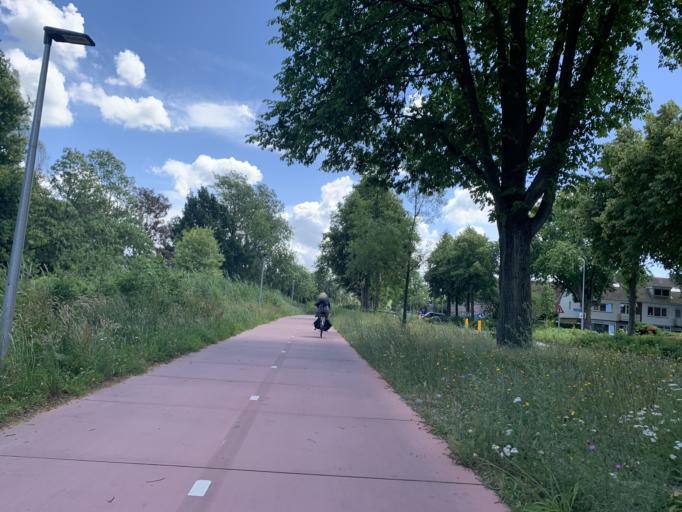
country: NL
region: Groningen
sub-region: Gemeente Groningen
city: Oosterpark
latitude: 53.1981
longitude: 6.5928
